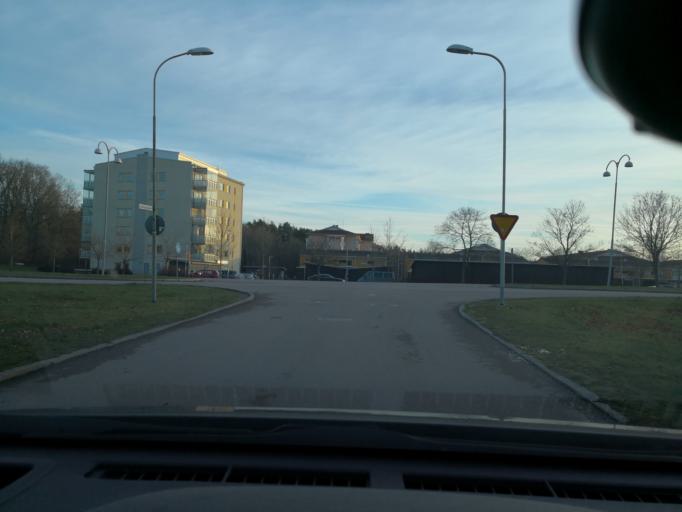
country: SE
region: Vaestmanland
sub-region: Vasteras
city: Vasteras
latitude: 59.6086
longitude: 16.4913
